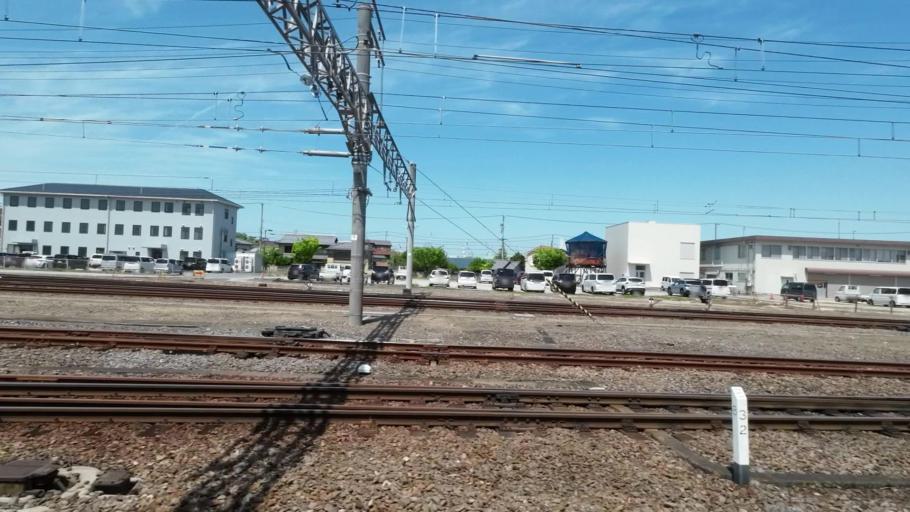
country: JP
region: Kagawa
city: Tadotsu
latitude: 34.2702
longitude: 133.7566
